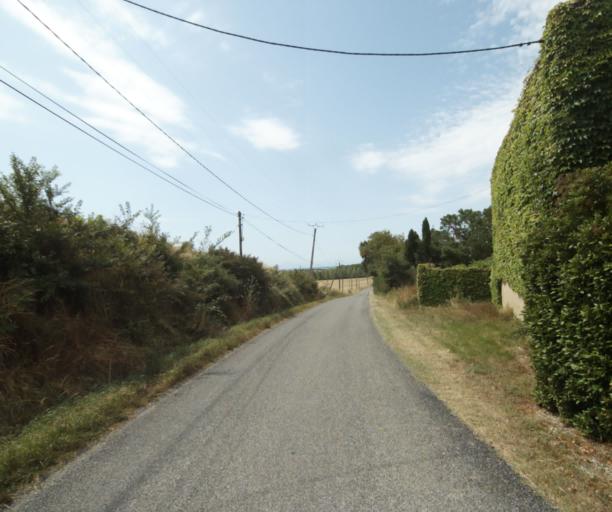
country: FR
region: Midi-Pyrenees
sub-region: Departement de la Haute-Garonne
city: Saint-Felix-Lauragais
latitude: 43.4291
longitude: 1.9195
